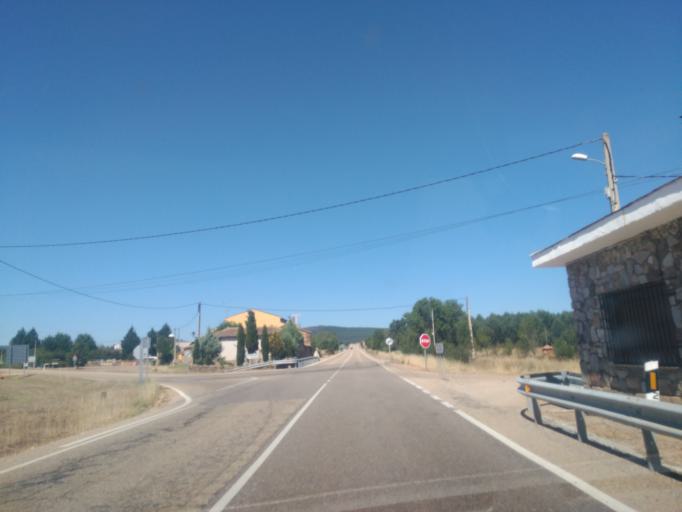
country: ES
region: Castille and Leon
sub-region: Provincia de Zamora
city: Ferreras de Abajo
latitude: 41.9023
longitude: -6.0585
